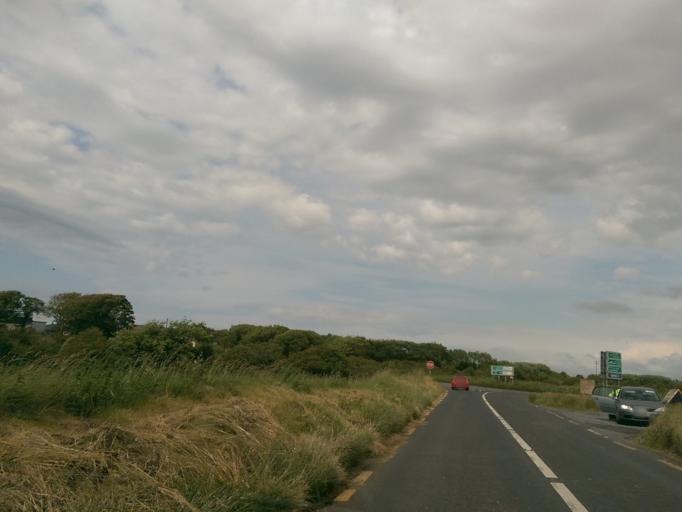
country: IE
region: Munster
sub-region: An Clar
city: Kilrush
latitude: 52.7855
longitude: -9.4399
